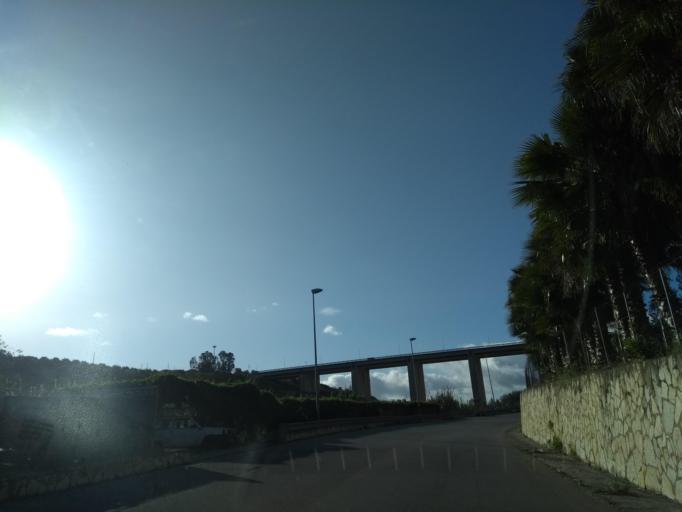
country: IT
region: Sicily
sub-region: Trapani
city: Alcamo
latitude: 38.0168
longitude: 12.9516
